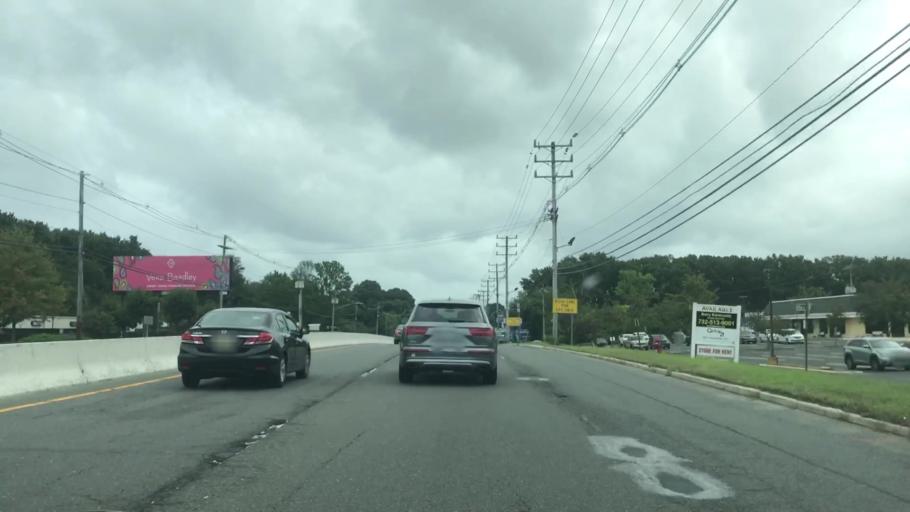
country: US
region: New Jersey
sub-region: Monmouth County
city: Oakhurst
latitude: 40.2571
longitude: -74.0406
